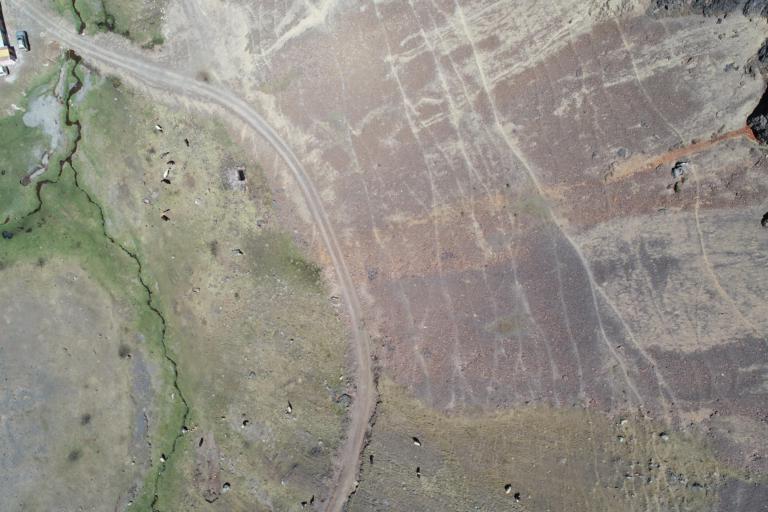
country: BO
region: La Paz
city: La Paz
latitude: -16.6199
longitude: -67.8277
